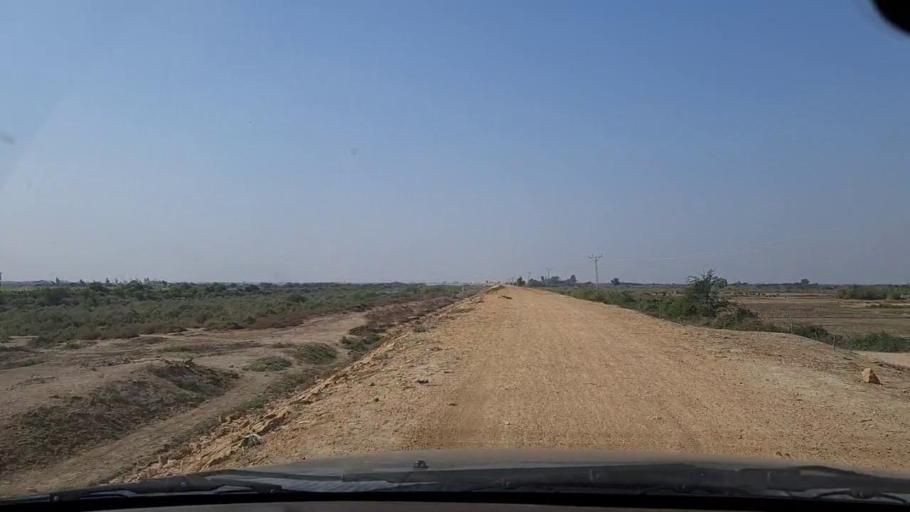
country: PK
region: Sindh
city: Chuhar Jamali
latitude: 24.4619
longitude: 67.8915
